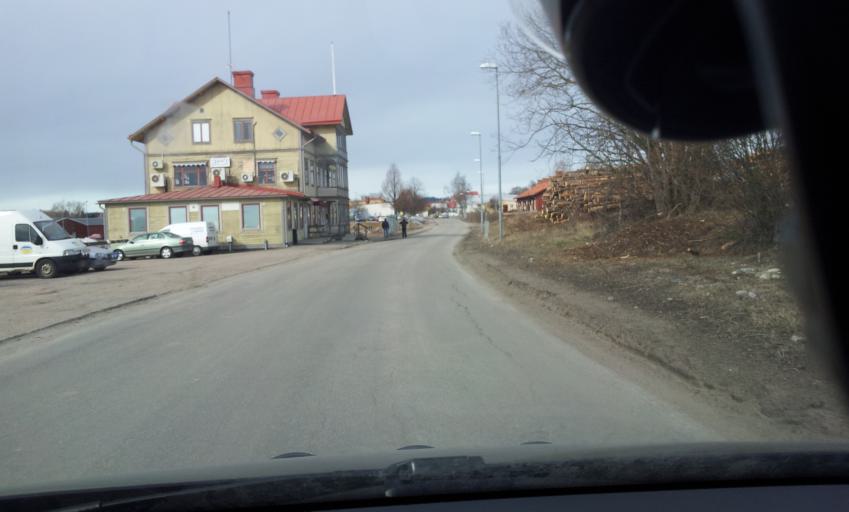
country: SE
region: Gaevleborg
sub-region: Ljusdals Kommun
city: Ljusdal
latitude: 61.8259
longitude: 16.0977
